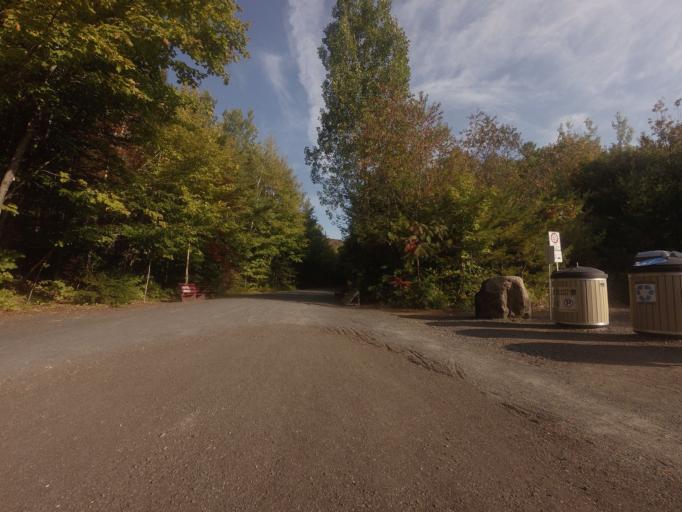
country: CA
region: Quebec
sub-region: Laurentides
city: Sainte-Adele
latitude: 45.9916
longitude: -74.1179
